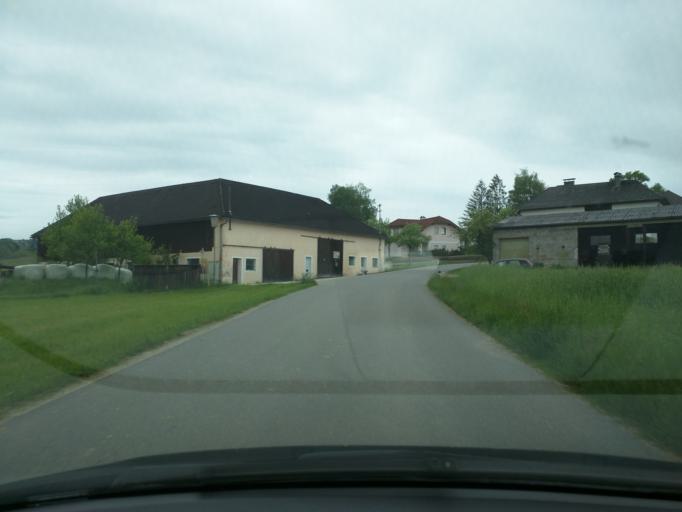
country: AT
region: Lower Austria
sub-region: Politischer Bezirk Melk
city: Blindenmarkt
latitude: 48.1395
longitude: 14.9744
